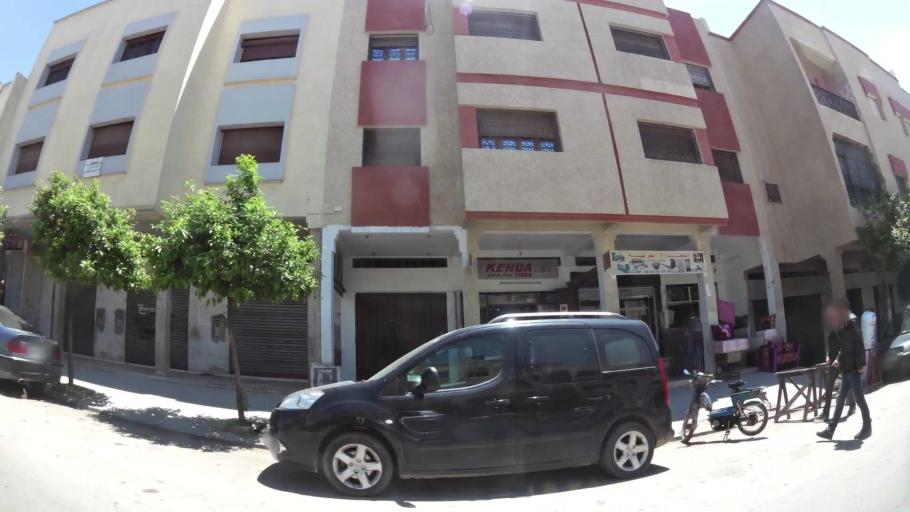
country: MA
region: Fes-Boulemane
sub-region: Fes
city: Fes
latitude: 34.0089
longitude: -4.9803
